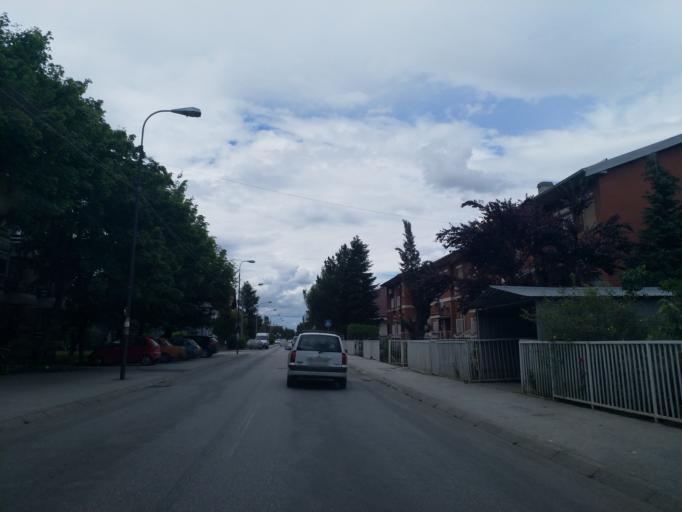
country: RS
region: Central Serbia
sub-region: Pomoravski Okrug
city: Jagodina
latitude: 43.9701
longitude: 21.2750
